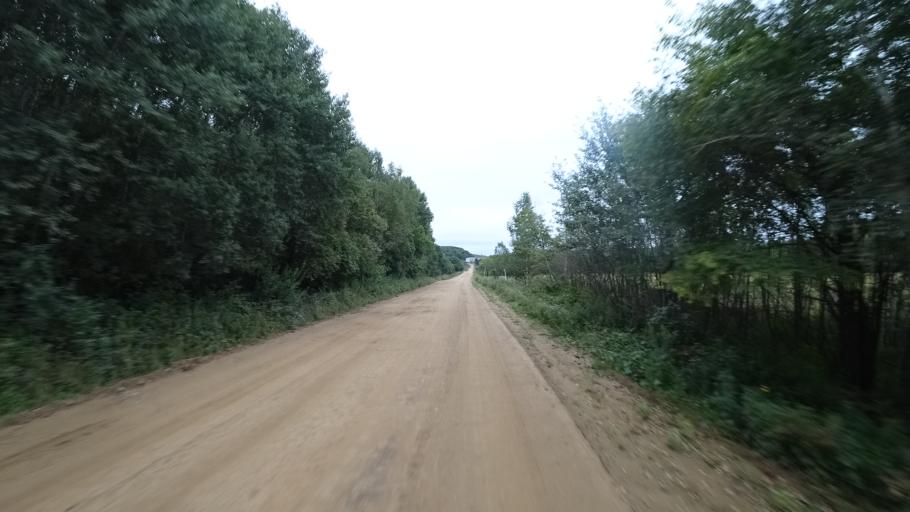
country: RU
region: Primorskiy
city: Rettikhovka
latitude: 44.1797
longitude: 132.8748
